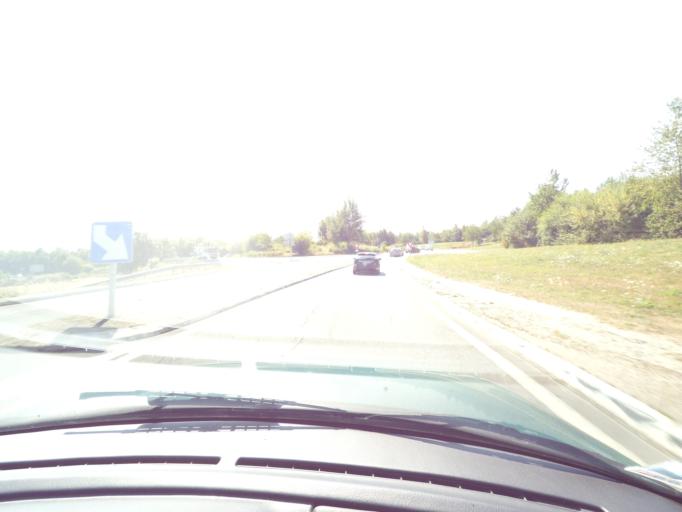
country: FR
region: Limousin
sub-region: Departement de la Haute-Vienne
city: Couzeix
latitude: 45.9026
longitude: 1.2250
